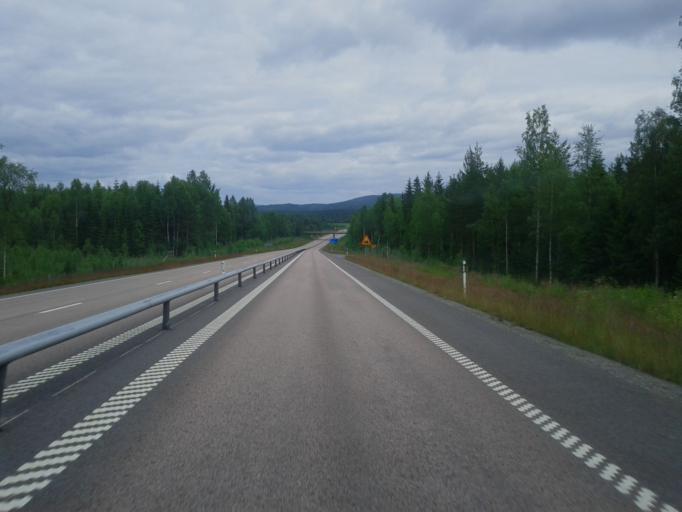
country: SE
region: Vaesternorrland
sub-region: OErnskoeldsviks Kommun
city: Bjasta
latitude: 63.2019
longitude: 18.4797
